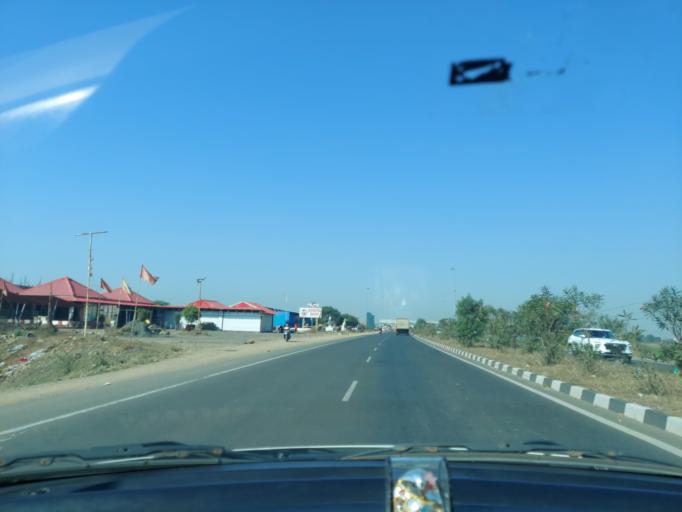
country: IN
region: Madhya Pradesh
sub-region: Indore
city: Pithampur
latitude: 22.6119
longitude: 75.7807
